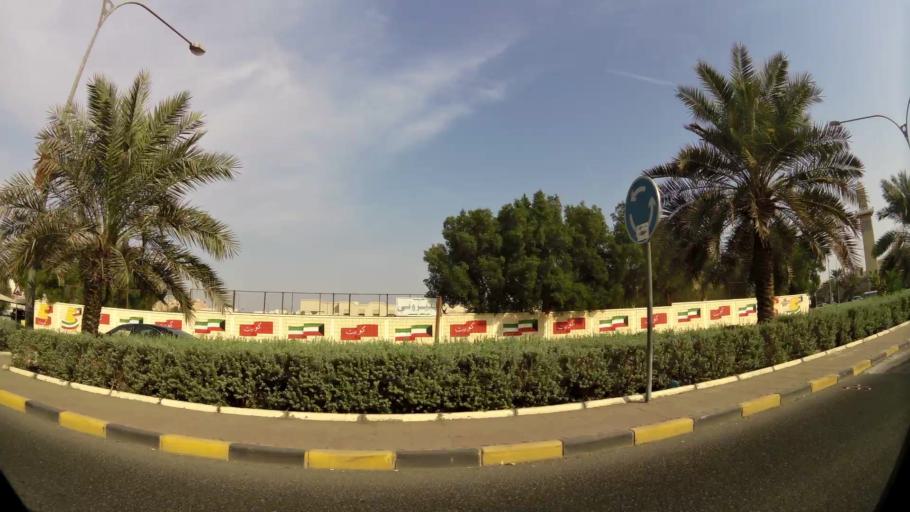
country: KW
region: Al Asimah
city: Ash Shamiyah
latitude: 29.3147
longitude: 47.9837
